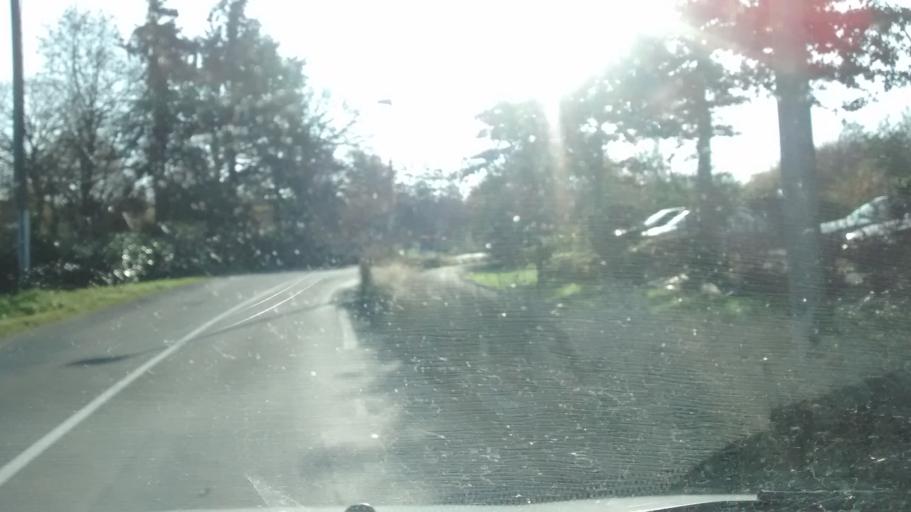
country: FR
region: Brittany
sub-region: Departement d'Ille-et-Vilaine
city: Pace
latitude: 48.1544
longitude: -1.7840
